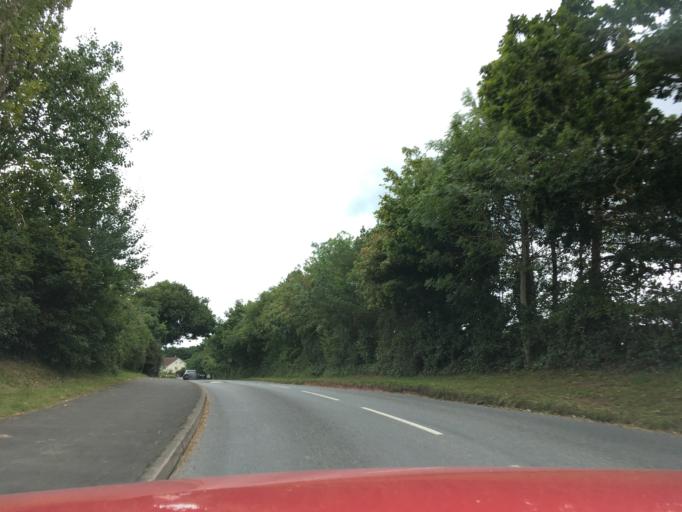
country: GB
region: England
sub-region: Devon
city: Dawlish
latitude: 50.5952
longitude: -3.4518
